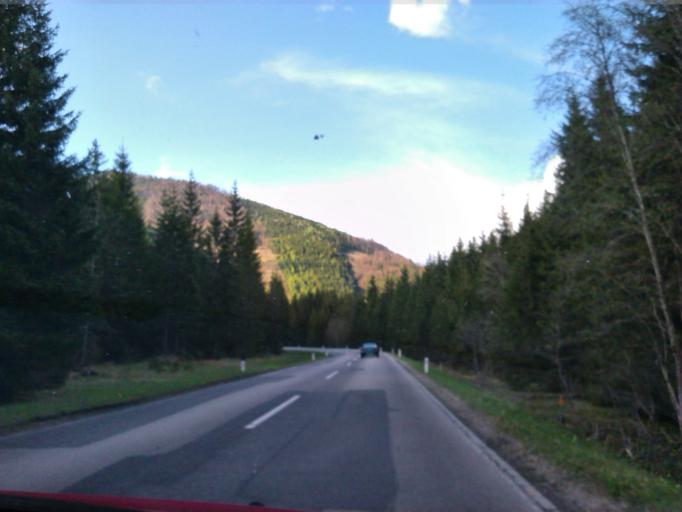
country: AT
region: Styria
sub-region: Politischer Bezirk Bruck-Muerzzuschlag
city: Muerzsteg
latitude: 47.7687
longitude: 15.5125
